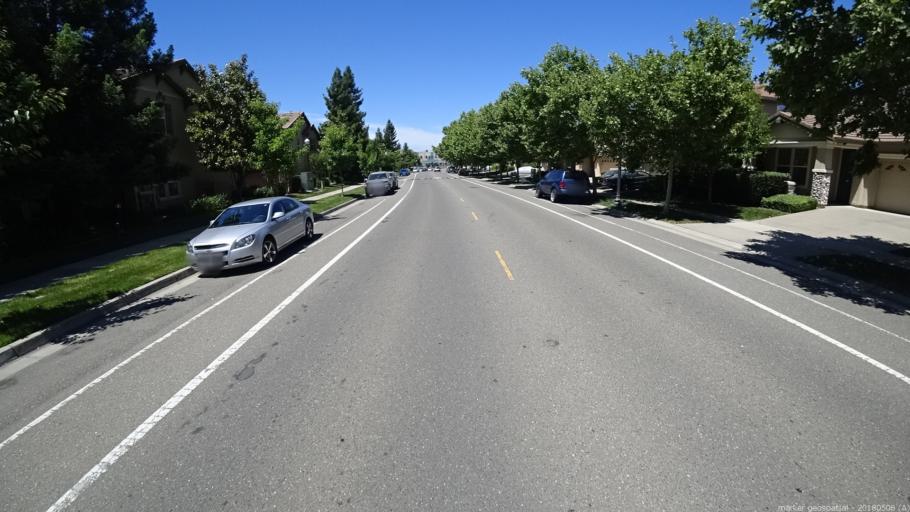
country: US
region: California
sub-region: Sacramento County
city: Elverta
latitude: 38.6648
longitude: -121.5297
